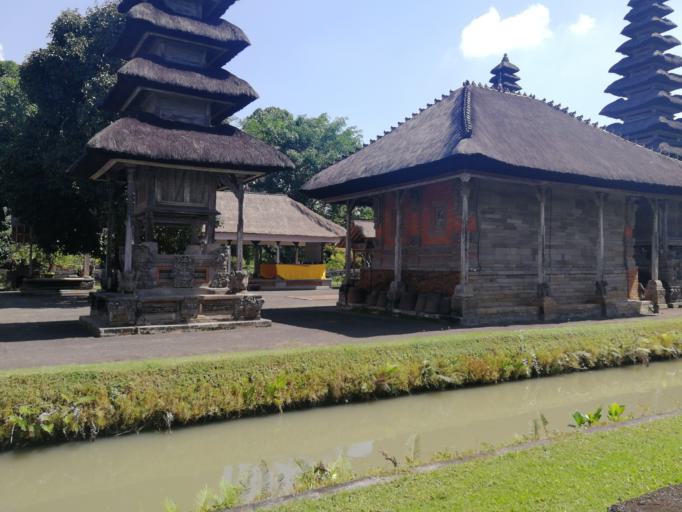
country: ID
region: Bali
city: Banjar Serangan
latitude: -8.5418
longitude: 115.1727
